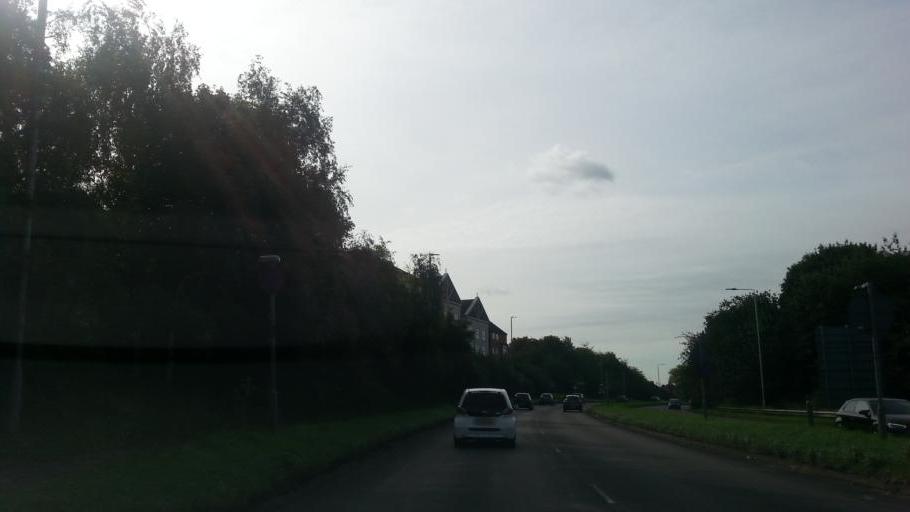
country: GB
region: England
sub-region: Leicestershire
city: Syston
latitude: 52.6839
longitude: -1.0932
